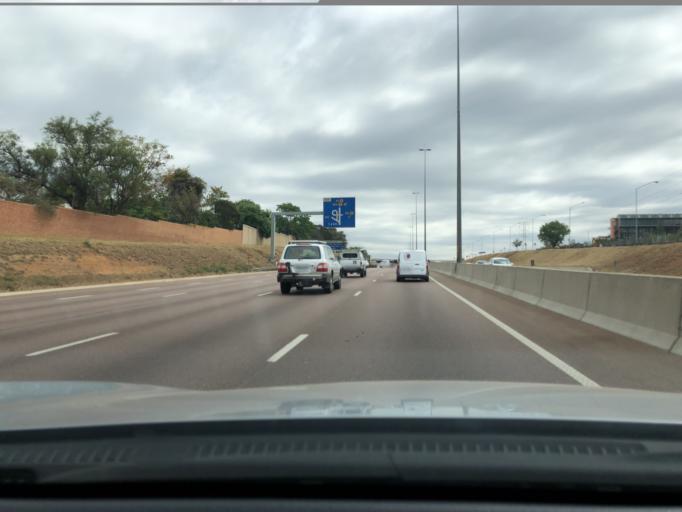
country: ZA
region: Gauteng
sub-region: City of Tshwane Metropolitan Municipality
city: Pretoria
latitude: -25.7604
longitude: 28.2751
